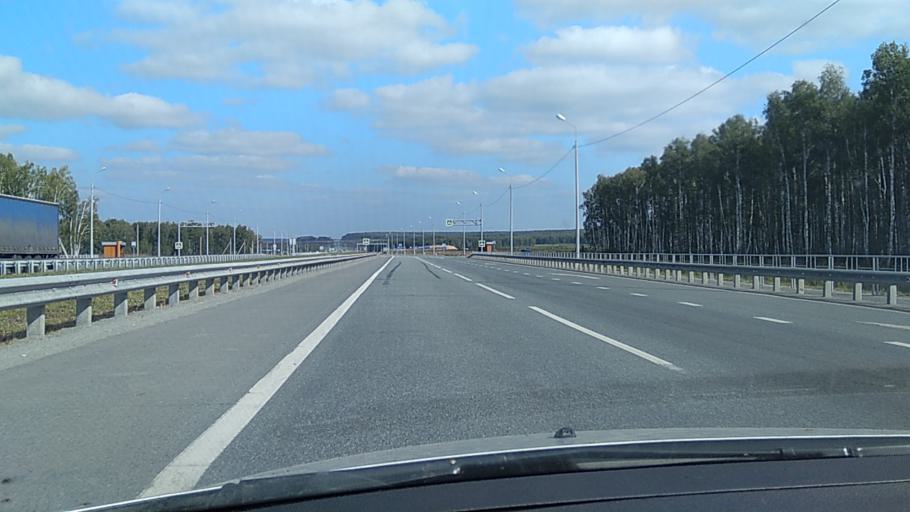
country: RU
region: Chelyabinsk
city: Chebarkul'
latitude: 54.9101
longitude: 60.4232
